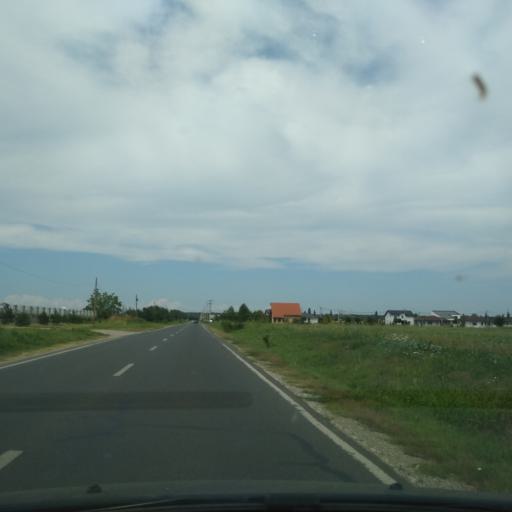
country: RO
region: Ilfov
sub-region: Comuna Balotesti
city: Balotesti
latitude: 44.6128
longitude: 26.1278
